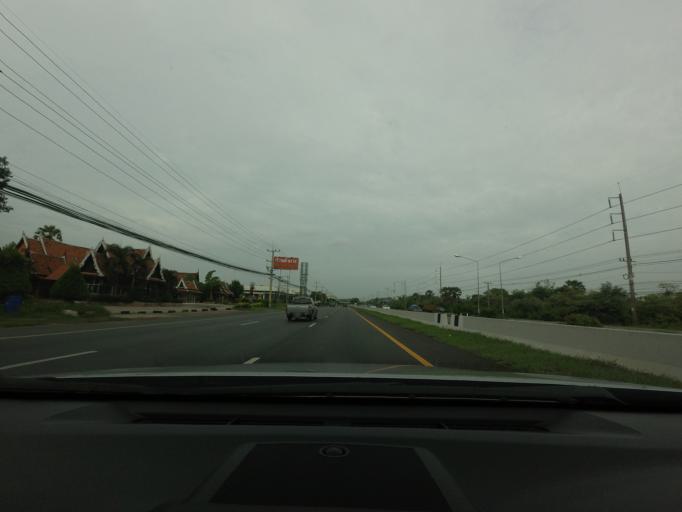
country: TH
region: Phetchaburi
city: Phetchaburi
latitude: 13.1202
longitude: 99.8976
